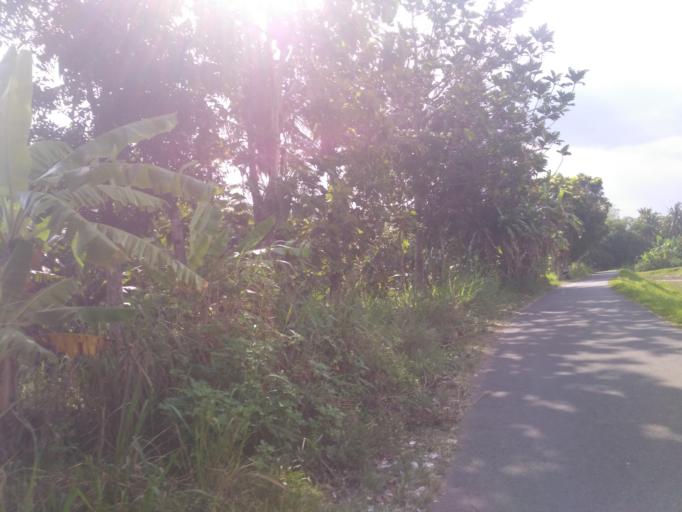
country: ID
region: Daerah Istimewa Yogyakarta
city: Godean
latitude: -7.7436
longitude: 110.3176
